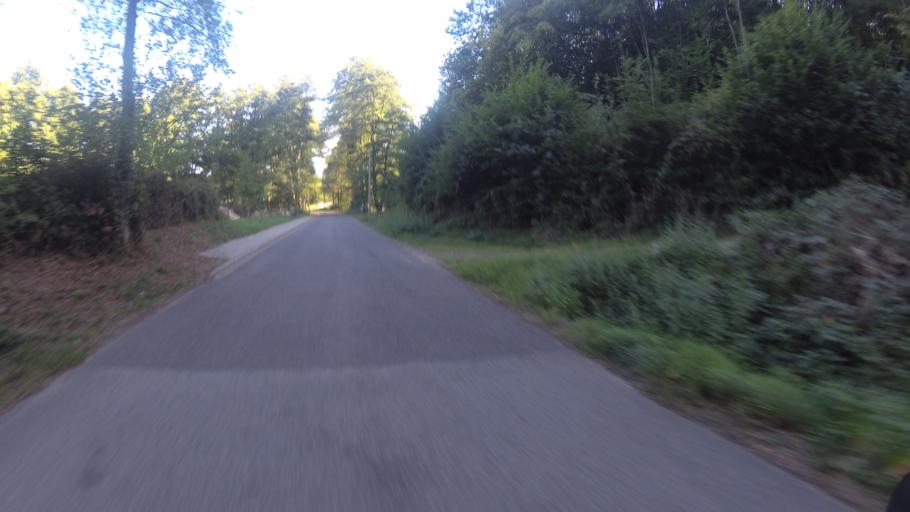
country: DE
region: Saarland
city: Lebach
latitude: 49.4395
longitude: 6.9430
